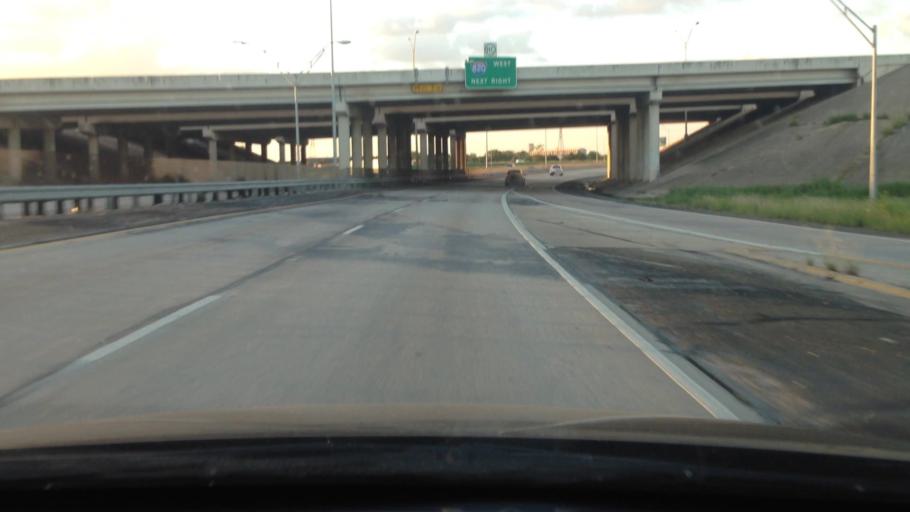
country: US
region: Texas
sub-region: Tarrant County
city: Saginaw
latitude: 32.8357
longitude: -97.3626
